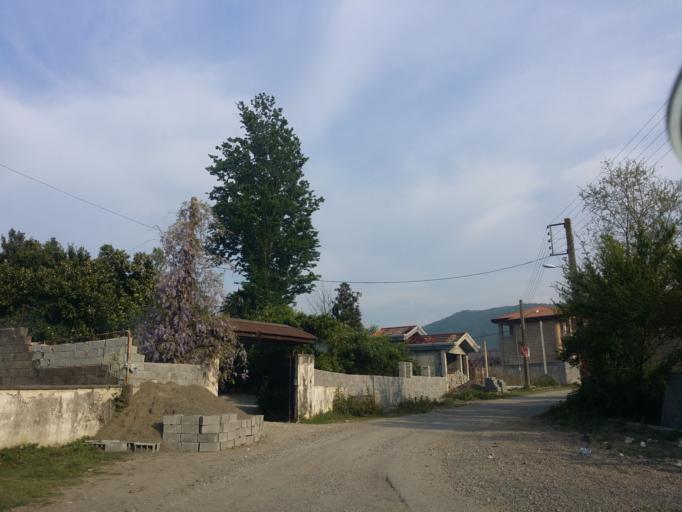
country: IR
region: Mazandaran
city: Chalus
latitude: 36.6607
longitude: 51.3665
